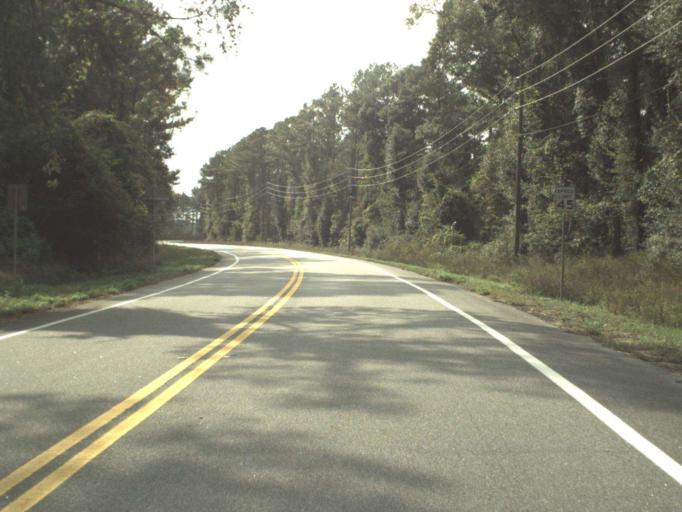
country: US
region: Florida
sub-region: Leon County
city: Woodville
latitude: 30.1995
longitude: -84.1851
